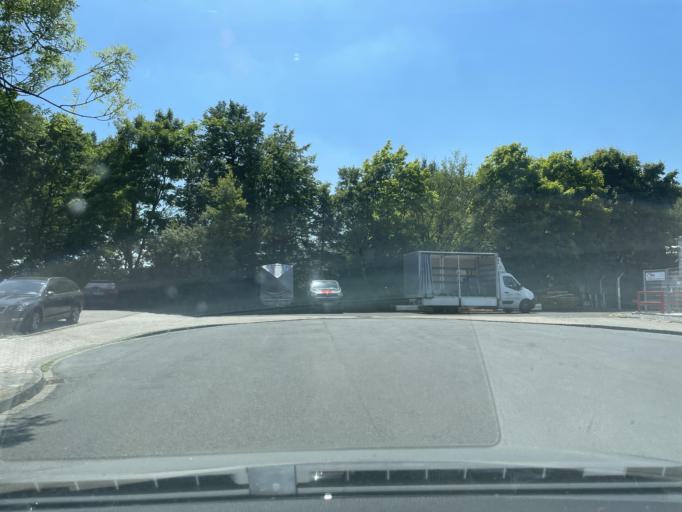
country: DE
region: North Rhine-Westphalia
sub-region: Regierungsbezirk Dusseldorf
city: Monchengladbach
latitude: 51.2290
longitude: 6.4687
